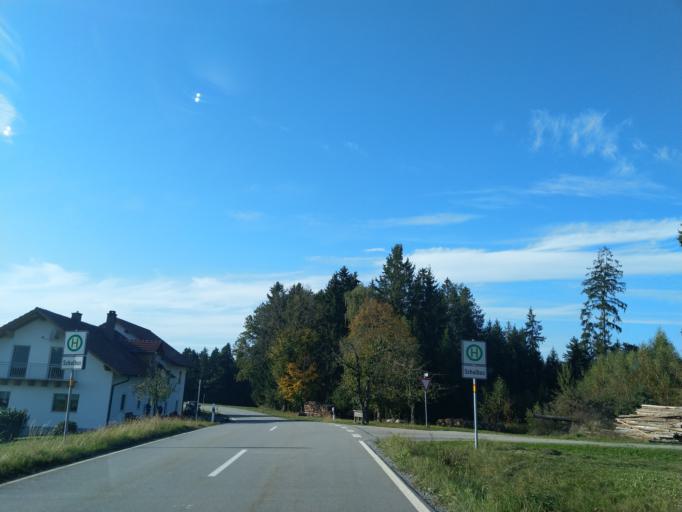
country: DE
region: Bavaria
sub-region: Lower Bavaria
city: Schwarzach
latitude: 48.9040
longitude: 12.8327
